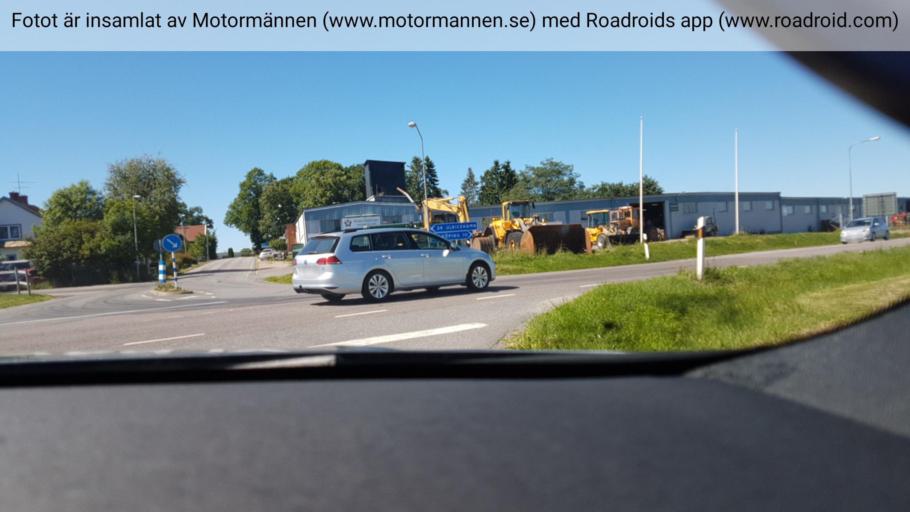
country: SE
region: Vaestra Goetaland
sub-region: Falkopings Kommun
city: Falkoeping
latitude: 58.0870
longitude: 13.5235
